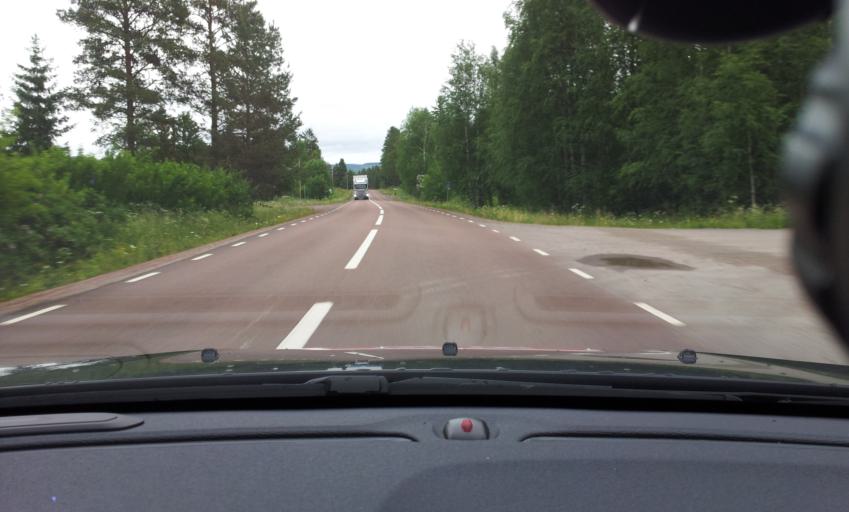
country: SE
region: Jaemtland
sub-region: Ragunda Kommun
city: Hammarstrand
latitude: 63.0186
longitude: 16.5729
